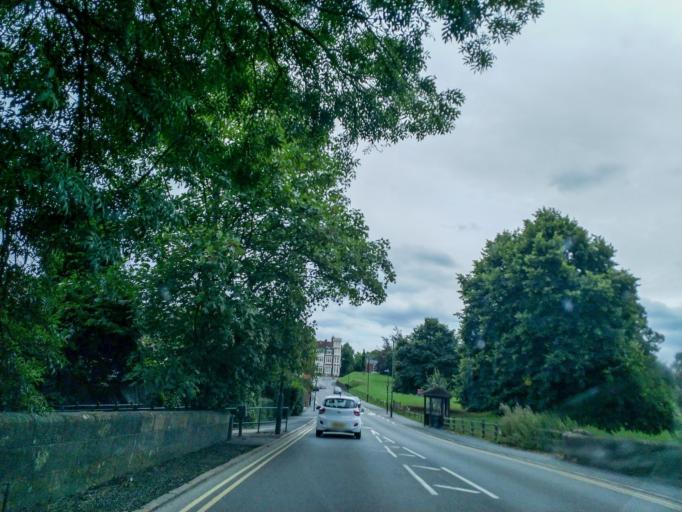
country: GB
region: England
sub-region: Warwickshire
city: Kenilworth
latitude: 52.3486
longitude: -1.5795
